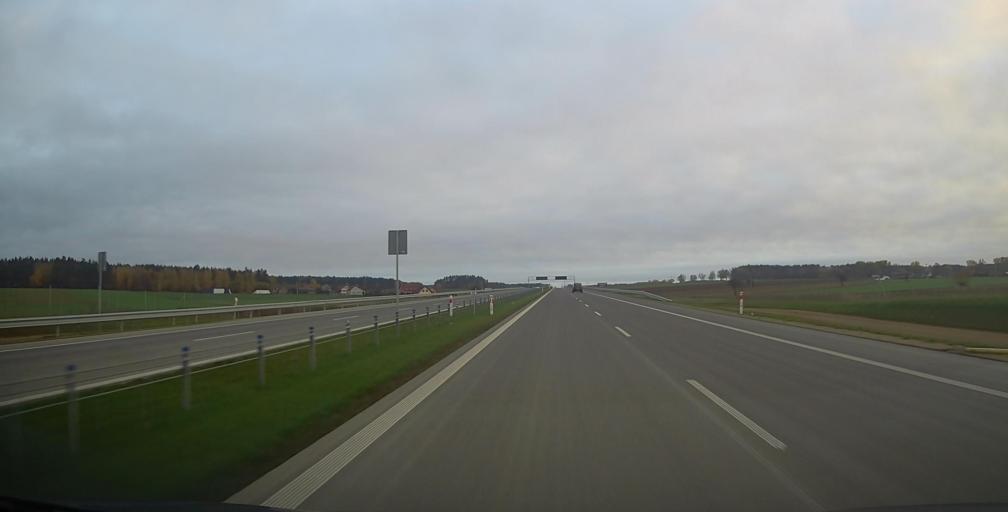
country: PL
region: Podlasie
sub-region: Powiat lomzynski
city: Piatnica
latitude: 53.2587
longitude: 22.1147
